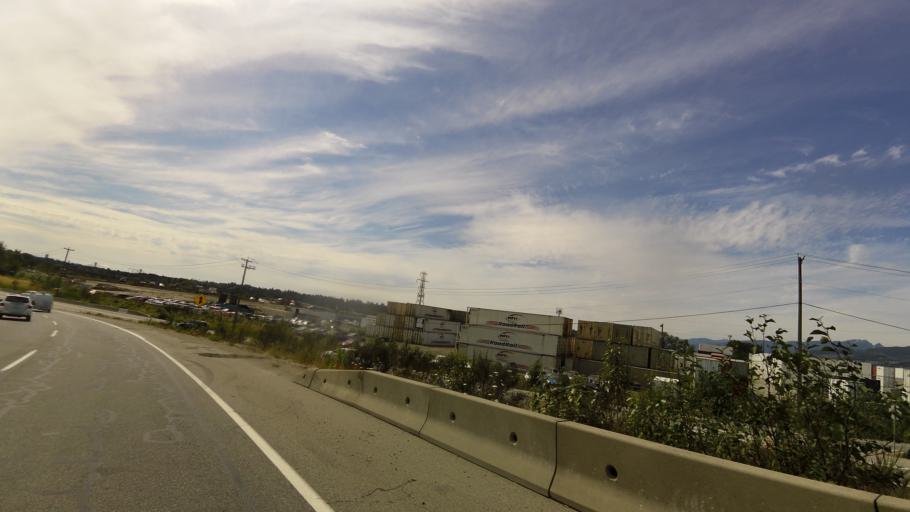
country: CA
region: British Columbia
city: Coquitlam
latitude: 49.2502
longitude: -122.7372
